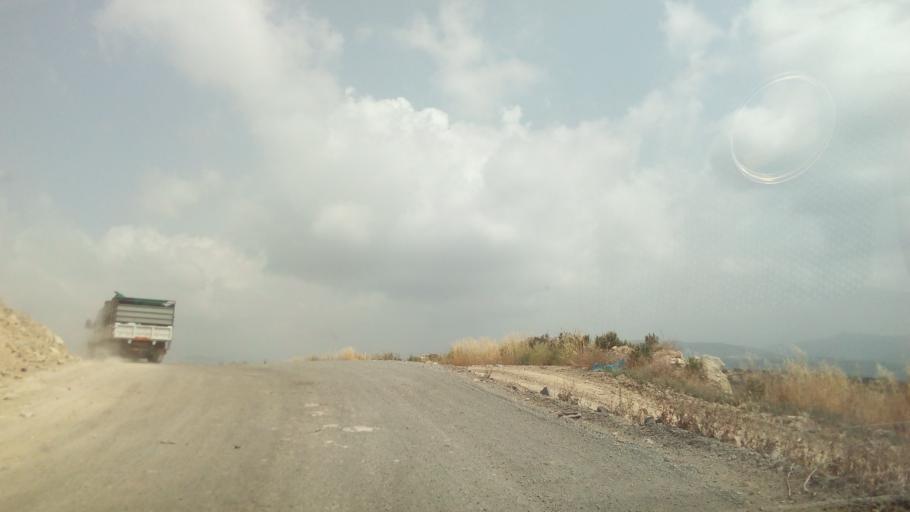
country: CY
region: Limassol
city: Pano Polemidia
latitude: 34.7456
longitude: 32.9519
